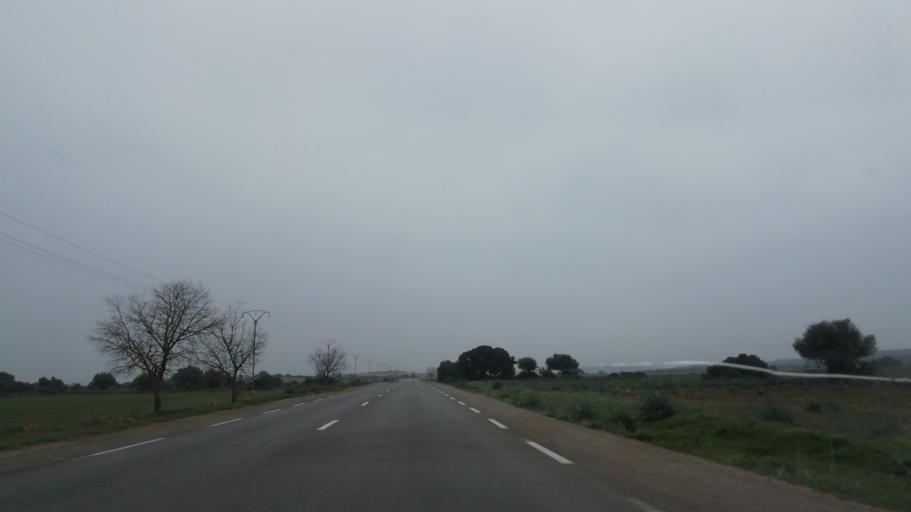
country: DZ
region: Mascara
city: Oued el Abtal
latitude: 35.3035
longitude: 0.4349
